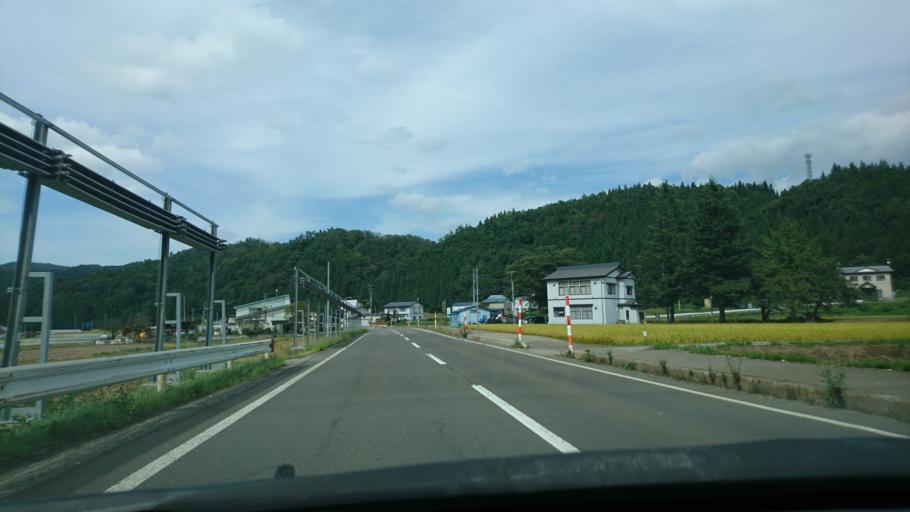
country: JP
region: Akita
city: Yuzawa
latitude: 39.1916
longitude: 140.6186
